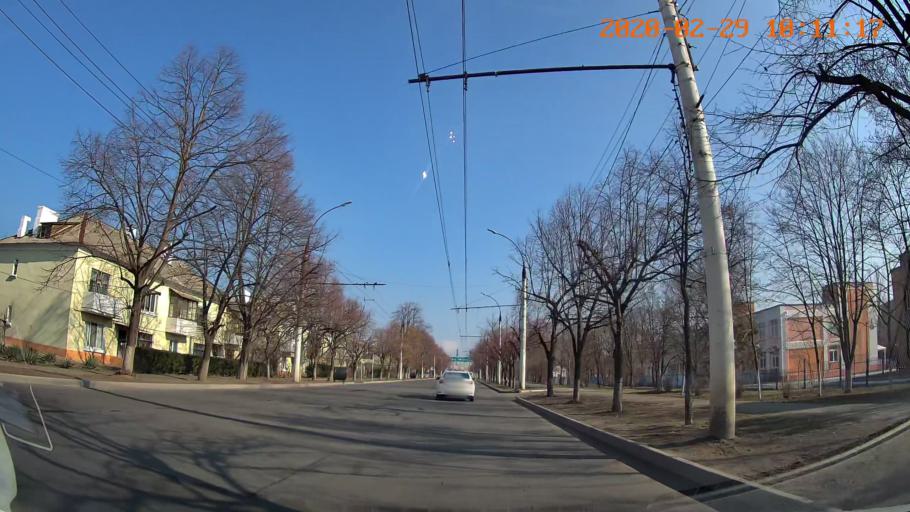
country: MD
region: Telenesti
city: Tiraspolul Nou
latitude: 46.8345
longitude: 29.6431
